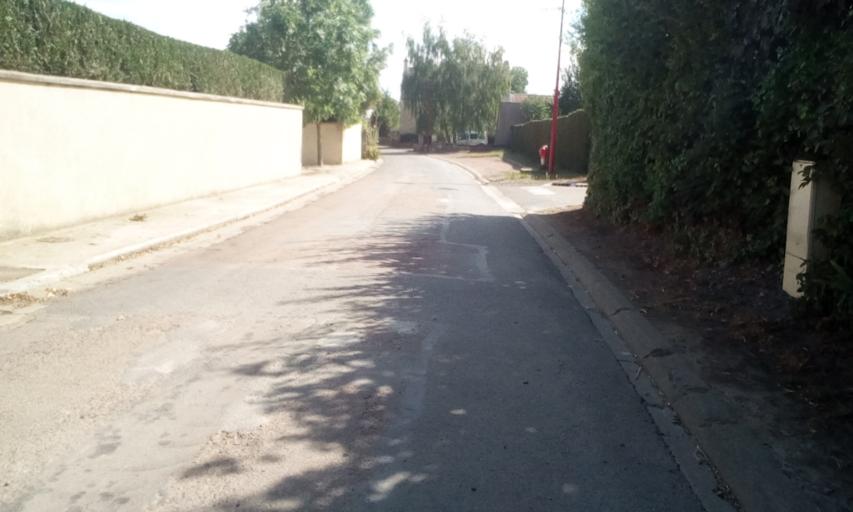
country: FR
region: Lower Normandy
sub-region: Departement du Calvados
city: Bully
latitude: 49.1101
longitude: -0.4366
